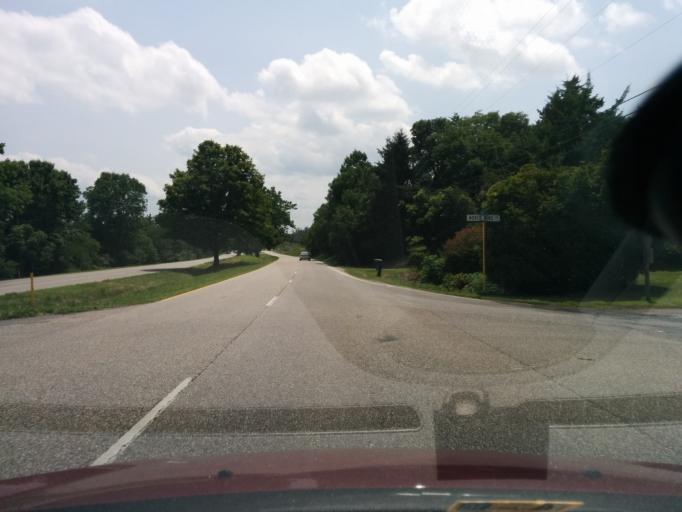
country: US
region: Virginia
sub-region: Rockbridge County
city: East Lexington
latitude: 37.8132
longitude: -79.3979
